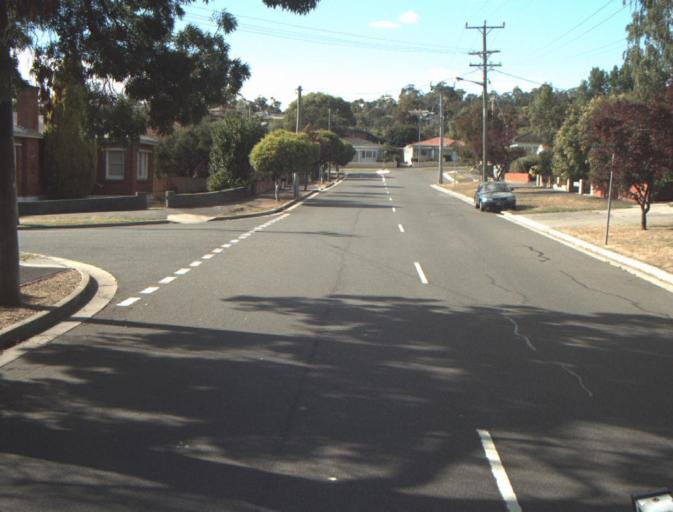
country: AU
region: Tasmania
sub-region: Launceston
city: East Launceston
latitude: -41.4497
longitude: 147.1593
